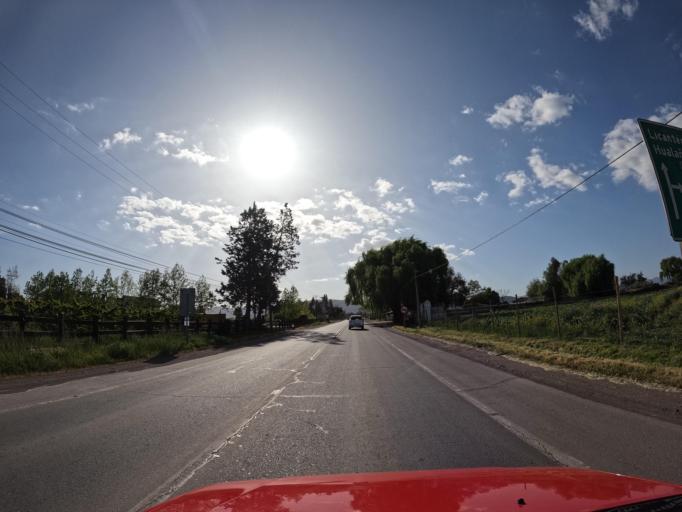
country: CL
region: Maule
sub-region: Provincia de Curico
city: Rauco
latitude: -34.9363
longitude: -71.2700
